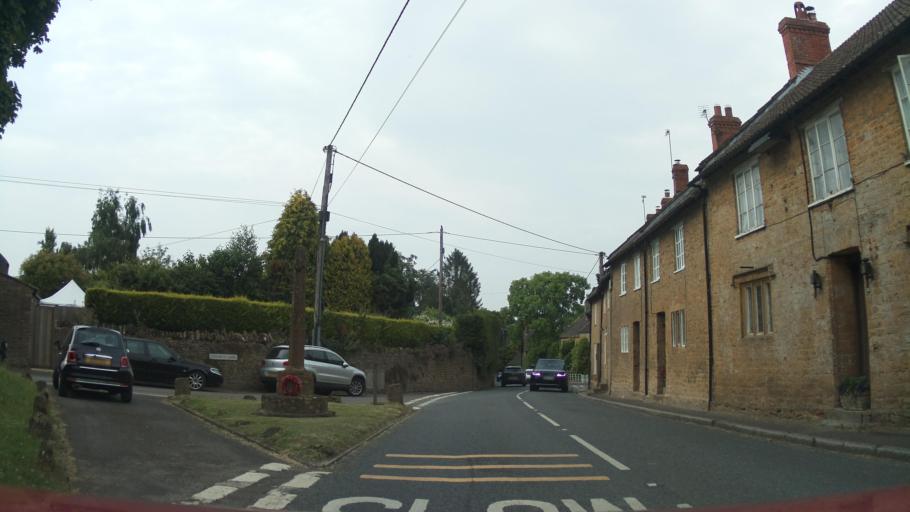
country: GB
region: England
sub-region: Somerset
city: Crewkerne
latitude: 50.8824
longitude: -2.7481
